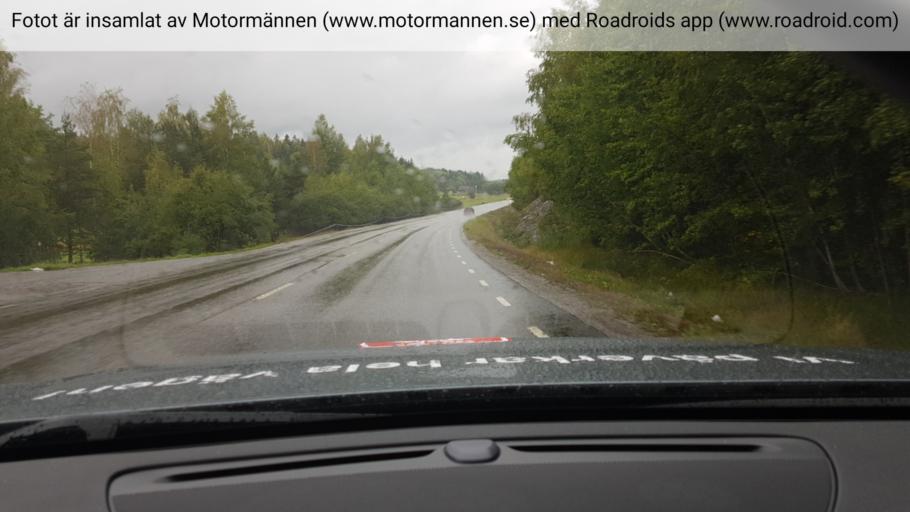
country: SE
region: Stockholm
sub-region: Haninge Kommun
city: Handen
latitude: 59.1945
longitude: 18.1185
